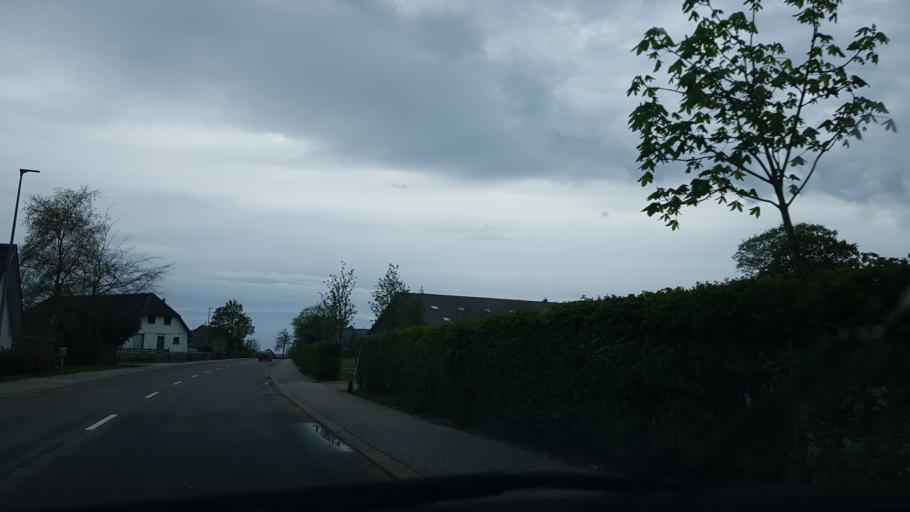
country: DK
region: South Denmark
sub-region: Kolding Kommune
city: Lunderskov
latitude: 55.4635
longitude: 9.3407
